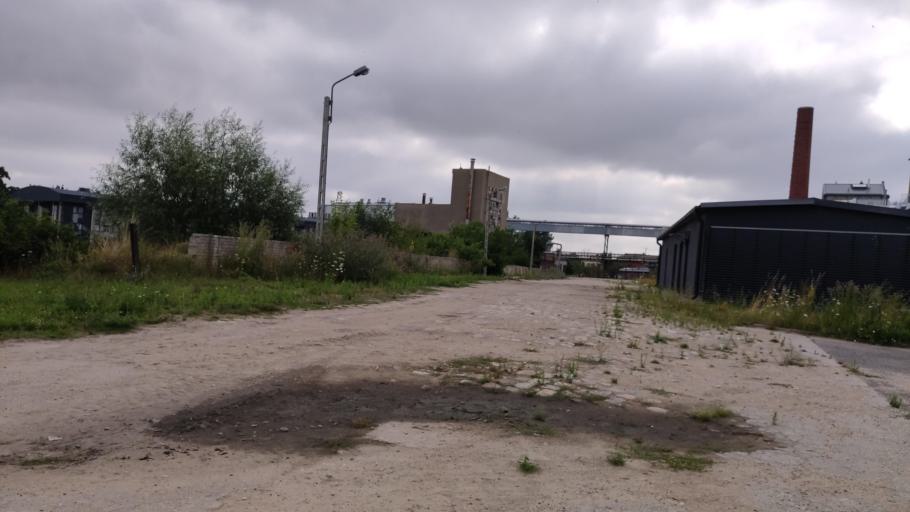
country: PL
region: Kujawsko-Pomorskie
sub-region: Powiat zninski
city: Znin
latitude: 52.8503
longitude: 17.7357
